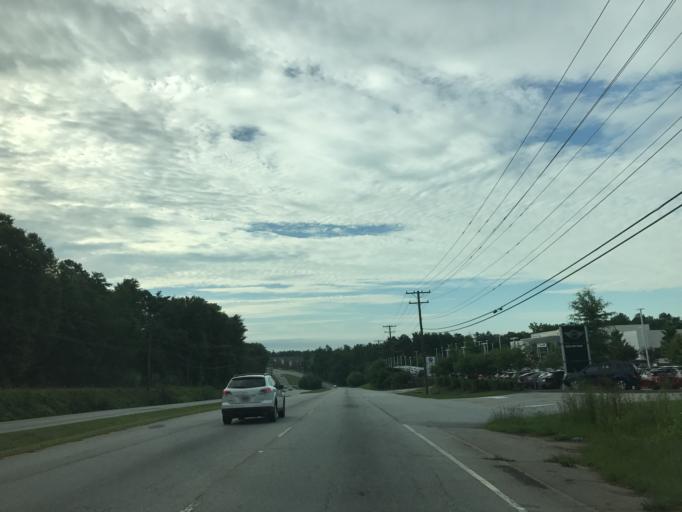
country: US
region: South Carolina
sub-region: Greenville County
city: Mauldin
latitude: 34.8086
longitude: -82.3314
